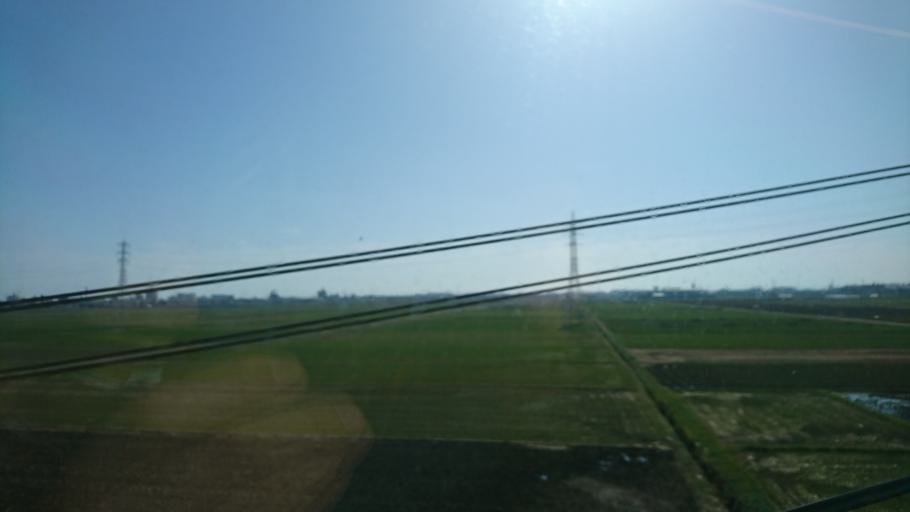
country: JP
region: Miyagi
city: Rifu
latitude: 38.2904
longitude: 140.9445
